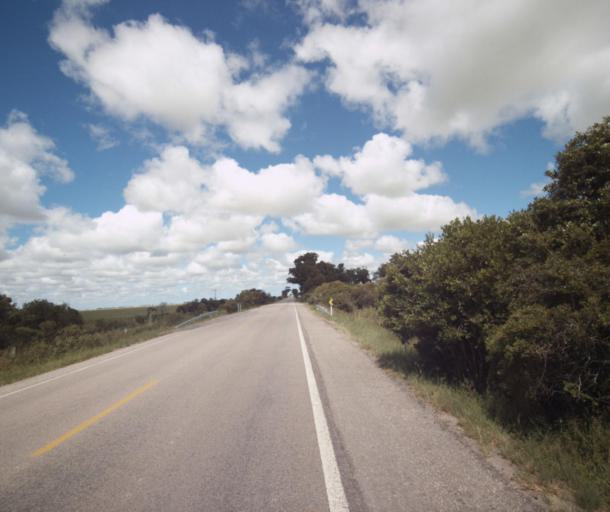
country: BR
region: Rio Grande do Sul
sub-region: Rio Grande
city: Rio Grande
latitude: -32.1836
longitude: -52.4263
